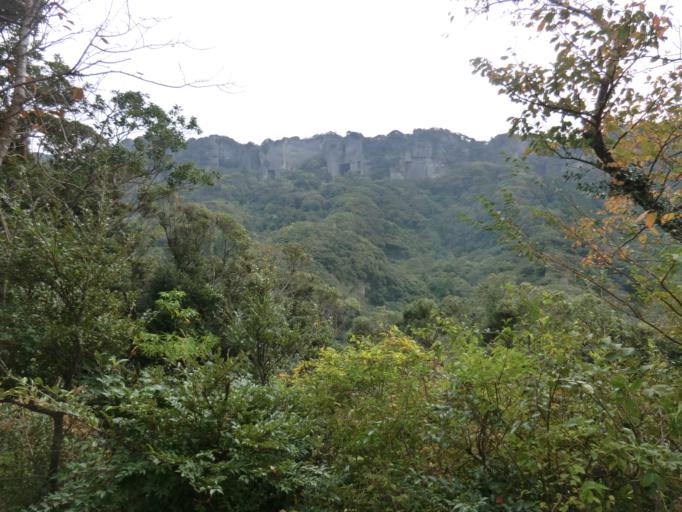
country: JP
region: Chiba
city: Futtsu
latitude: 35.1642
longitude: 139.8302
